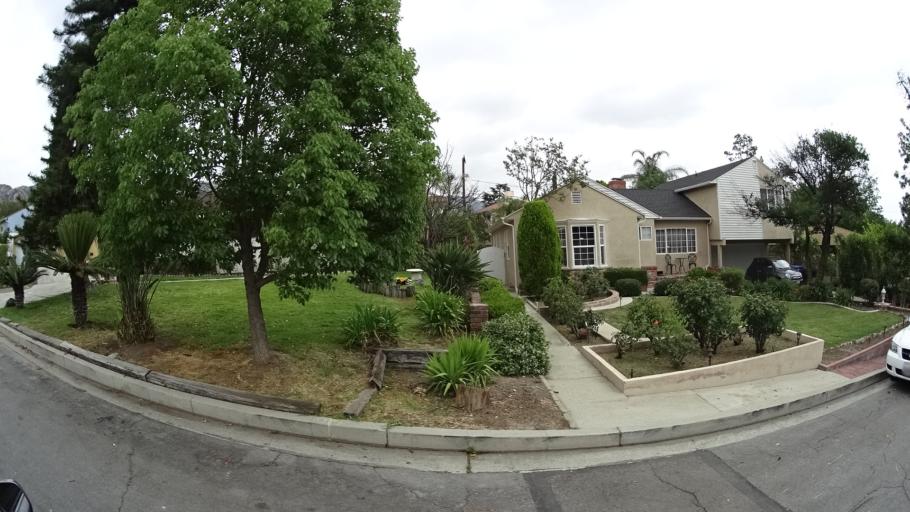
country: US
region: California
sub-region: Los Angeles County
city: Burbank
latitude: 34.2049
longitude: -118.3312
